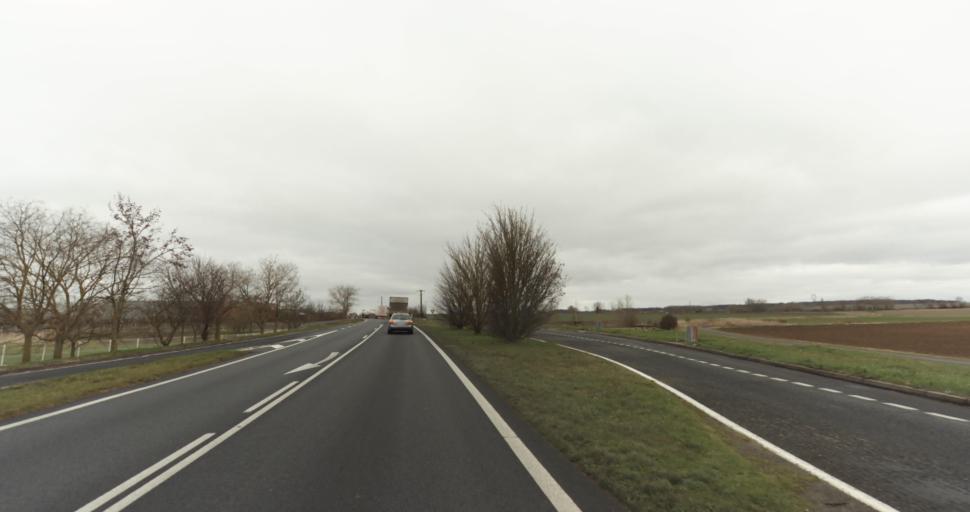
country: FR
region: Pays de la Loire
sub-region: Departement de Maine-et-Loire
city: Doue-la-Fontaine
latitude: 47.1887
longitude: -0.2432
